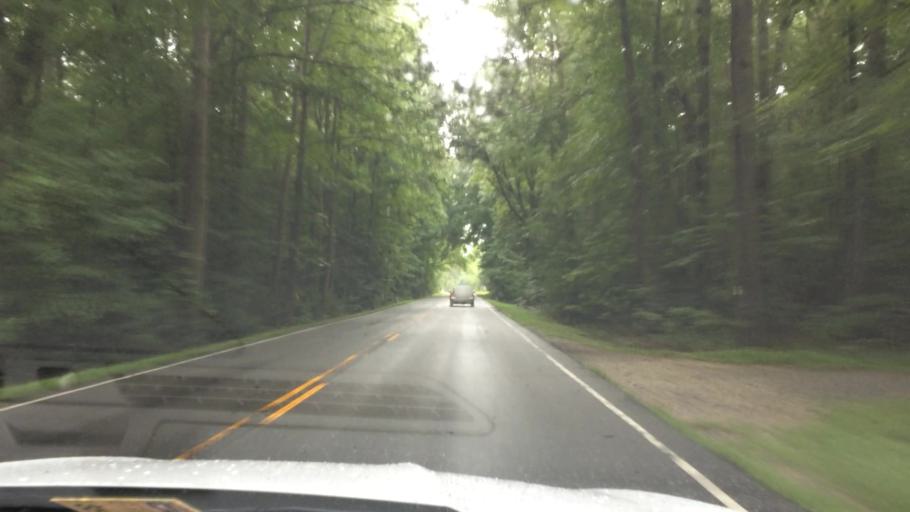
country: US
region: Virginia
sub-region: King William County
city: West Point
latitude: 37.4420
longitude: -76.8376
